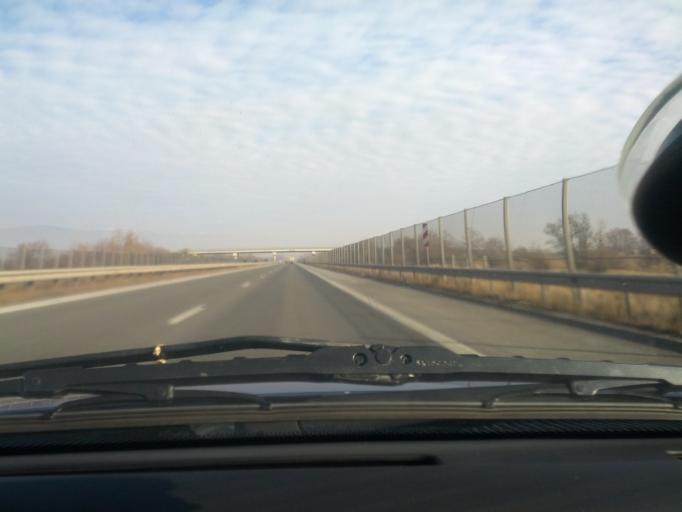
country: BG
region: Sofia-Capital
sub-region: Stolichna Obshtina
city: Bukhovo
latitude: 42.7101
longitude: 23.4692
